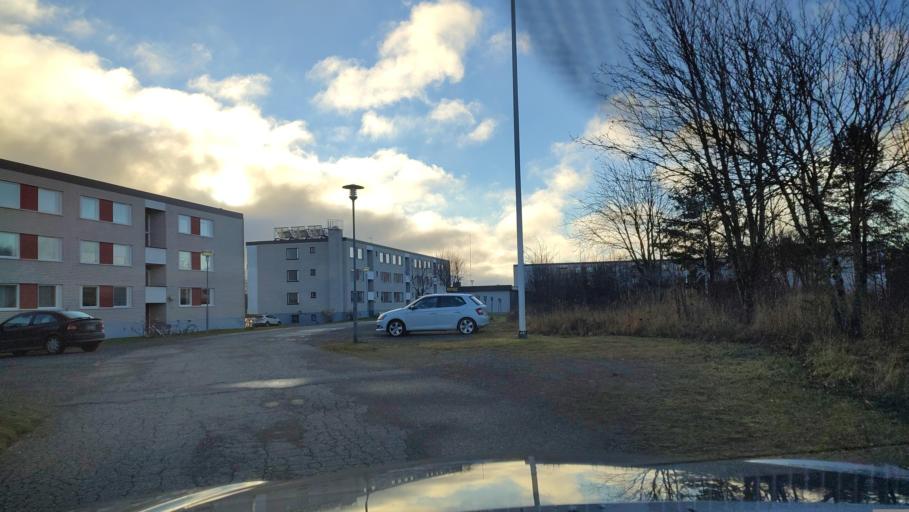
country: FI
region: Ostrobothnia
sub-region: Sydosterbotten
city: Kristinestad
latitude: 62.2677
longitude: 21.3770
